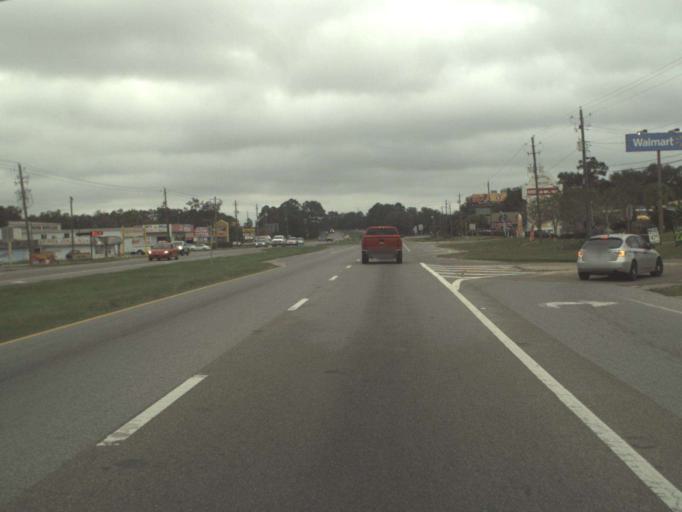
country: US
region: Florida
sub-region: Escambia County
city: Ensley
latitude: 30.5271
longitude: -87.2749
